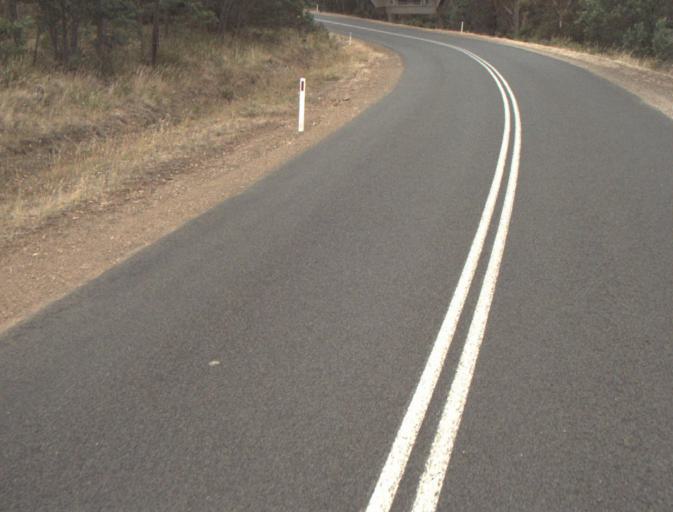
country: AU
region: Tasmania
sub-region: Northern Midlands
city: Evandale
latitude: -41.5140
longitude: 147.3342
